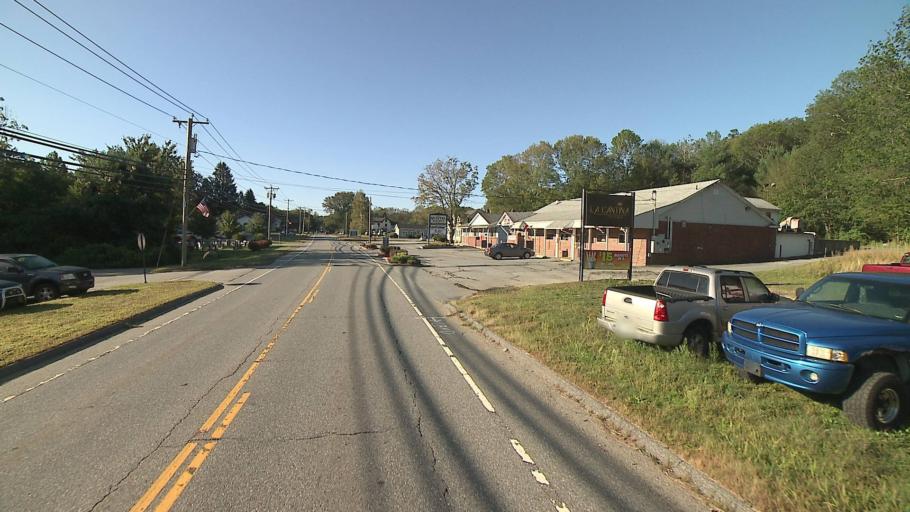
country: US
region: Connecticut
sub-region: Windham County
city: Moosup
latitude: 41.7113
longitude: -71.9048
